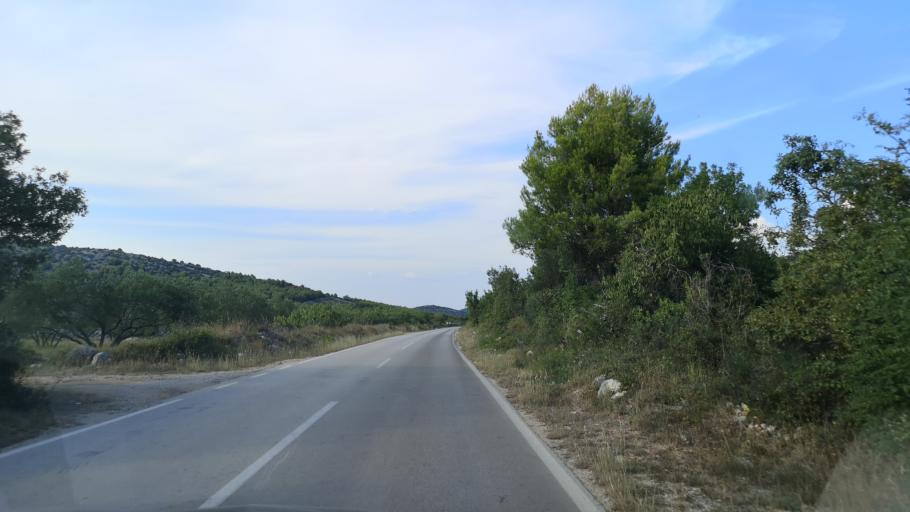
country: HR
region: Sibensko-Kniniska
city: Vodice
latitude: 43.7985
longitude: 15.7715
